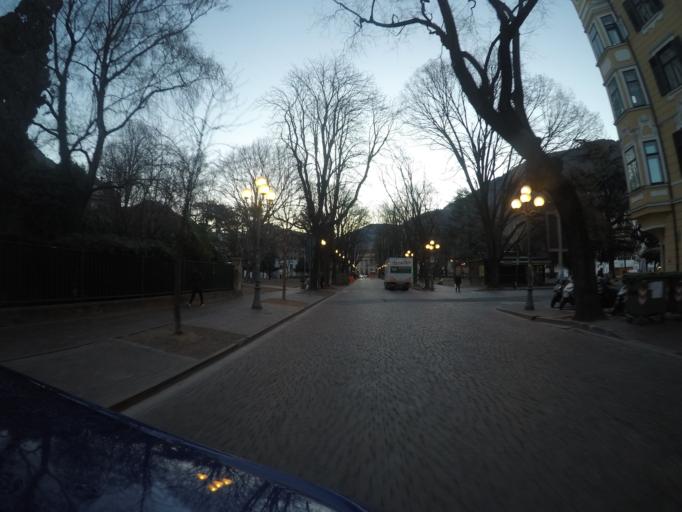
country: IT
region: Trentino-Alto Adige
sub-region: Bolzano
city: Bolzano
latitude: 46.4974
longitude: 11.3559
